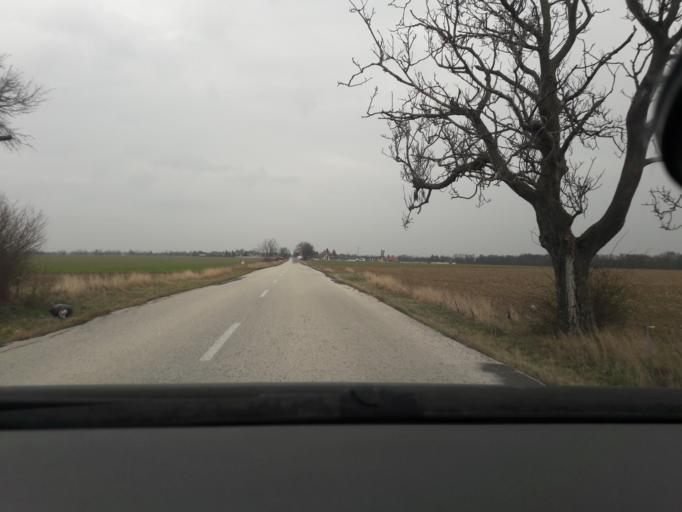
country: SK
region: Bratislavsky
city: Senec
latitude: 48.3233
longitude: 17.4345
